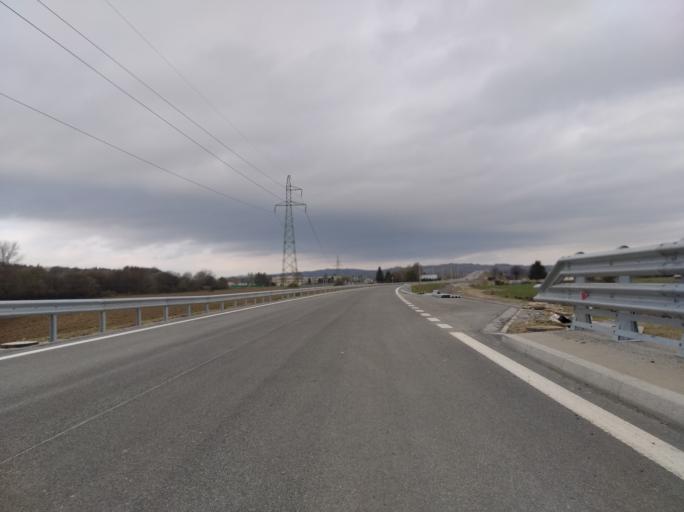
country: PL
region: Subcarpathian Voivodeship
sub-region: Powiat strzyzowski
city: Strzyzow
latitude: 49.8644
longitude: 21.7774
